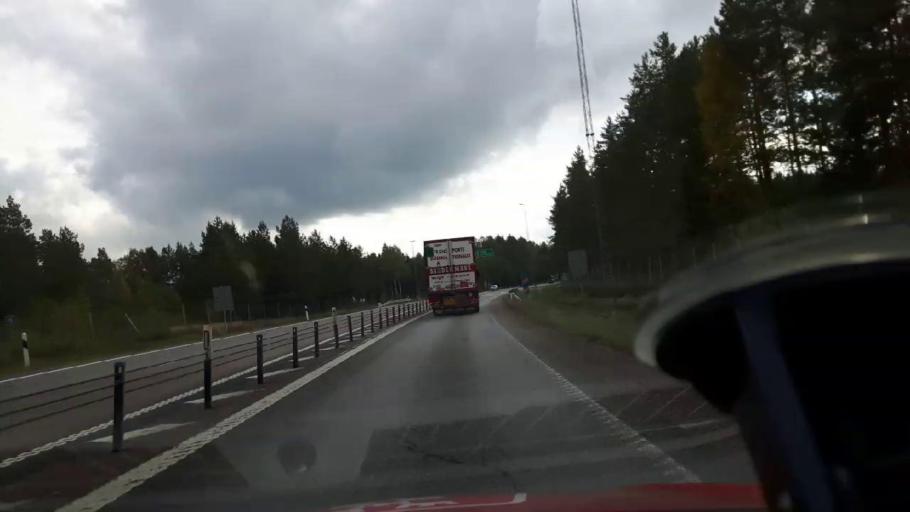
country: SE
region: Gaevleborg
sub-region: Gavle Kommun
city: Norrsundet
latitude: 60.9612
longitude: 17.0336
